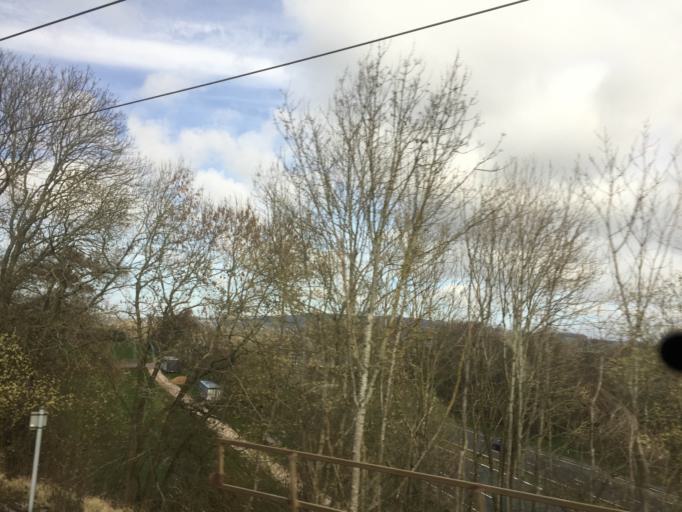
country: GB
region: England
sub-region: Cumbria
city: Penrith
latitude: 54.6350
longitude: -2.7285
